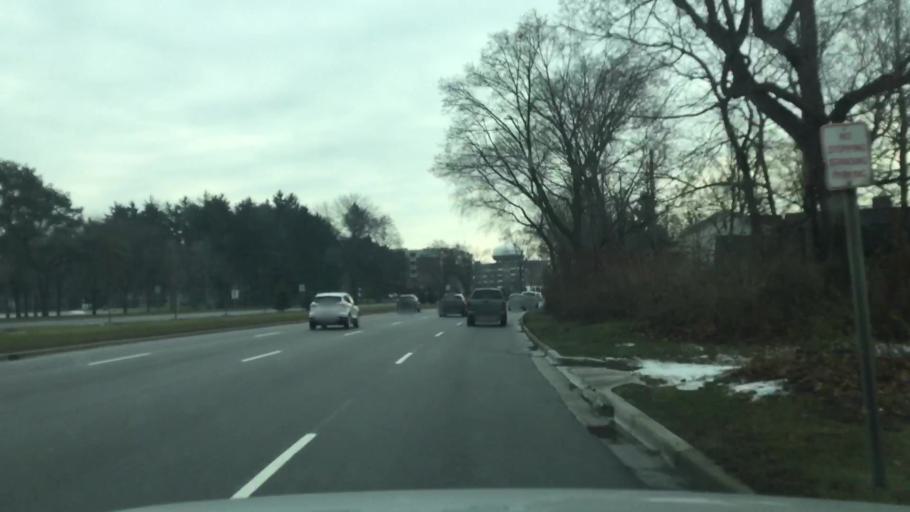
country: US
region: Michigan
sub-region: Oakland County
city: Birmingham
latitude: 42.5518
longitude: -83.2152
